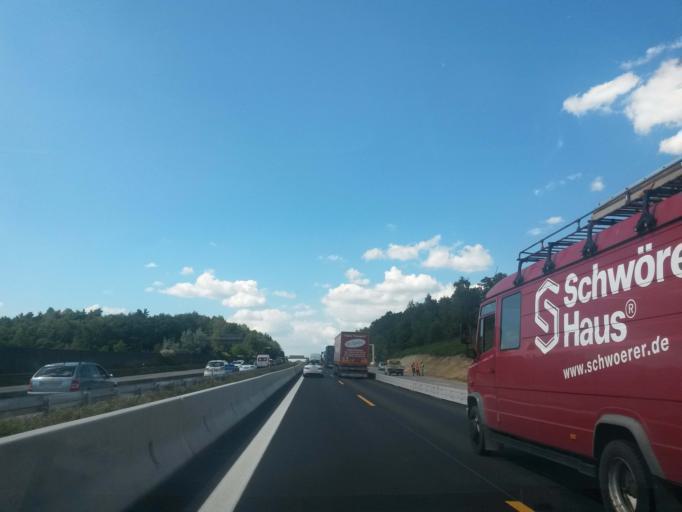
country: DE
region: Bavaria
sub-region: Upper Bavaria
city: Paunzhausen
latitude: 48.4665
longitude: 11.5878
